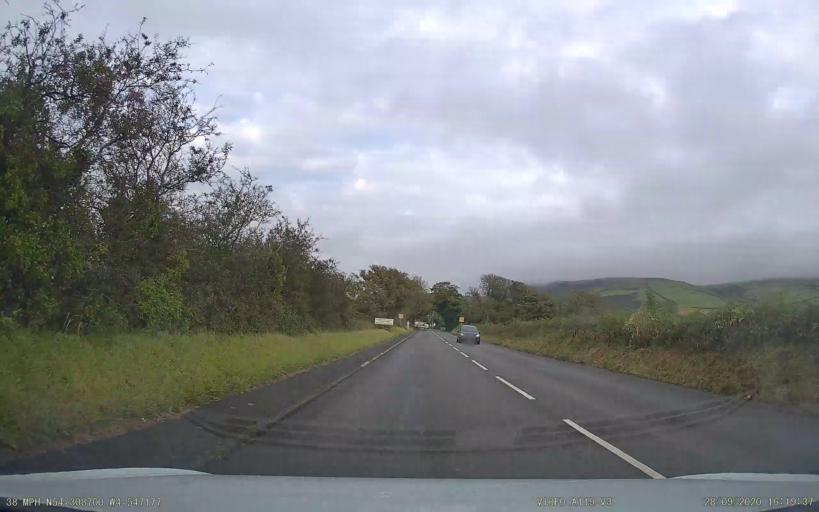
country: IM
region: Ramsey
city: Ramsey
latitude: 54.3087
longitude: -4.5472
